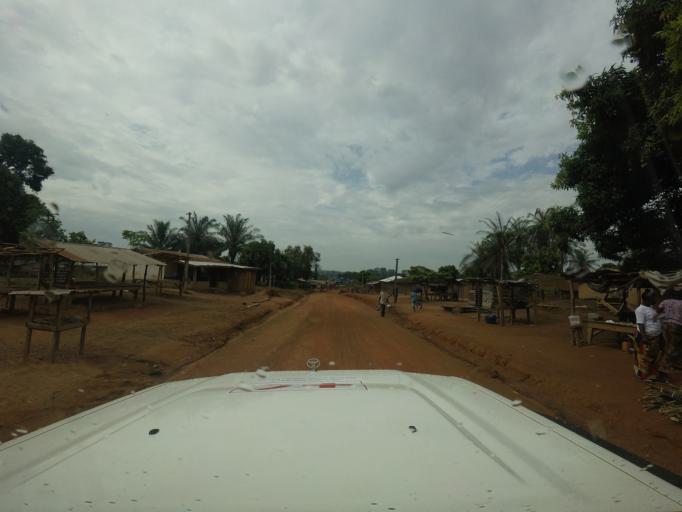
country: SL
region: Eastern Province
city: Buedu
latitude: 8.3542
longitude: -10.2079
